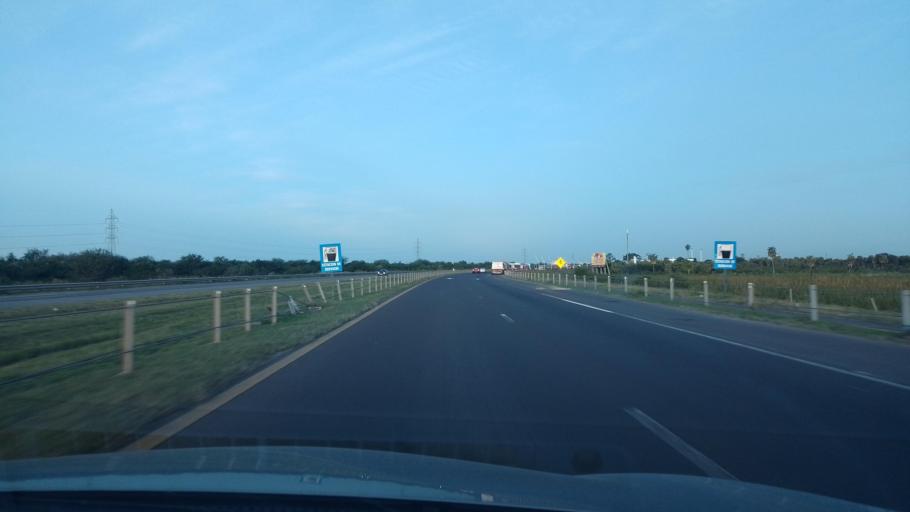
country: AR
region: Chaco
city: Barranqueras
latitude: -27.4376
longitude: -58.8996
